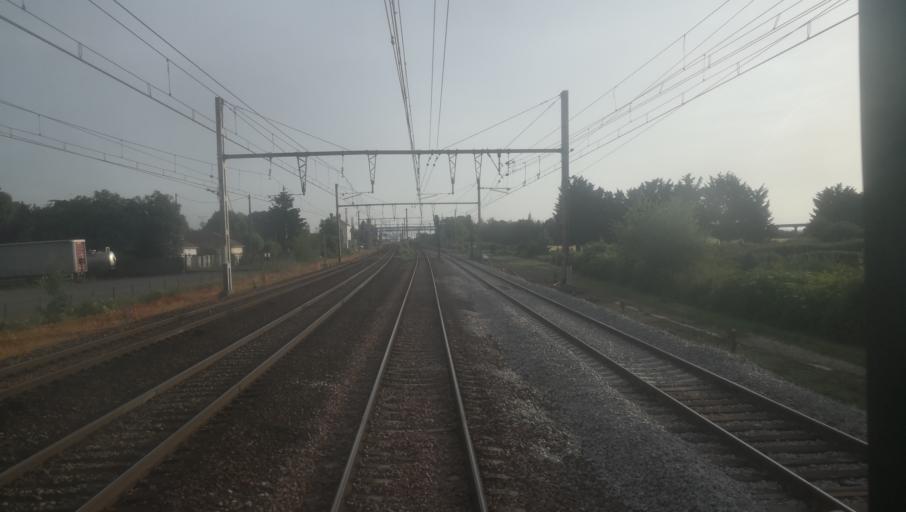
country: FR
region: Centre
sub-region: Departement du Loiret
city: Artenay
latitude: 48.0789
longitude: 1.8825
